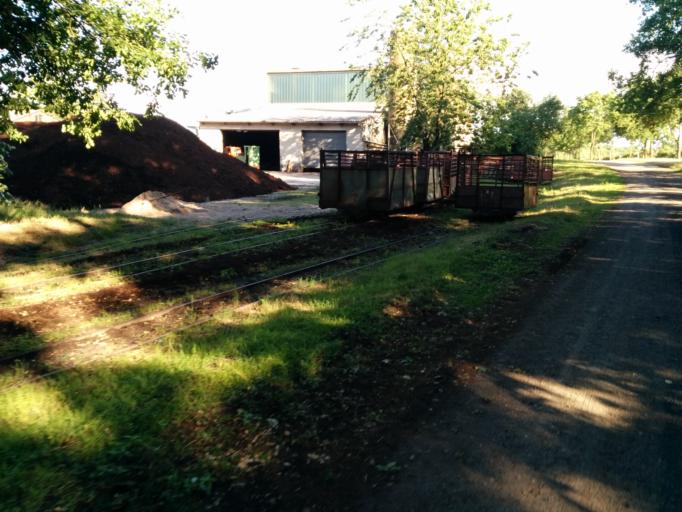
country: DE
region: Lower Saxony
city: Lohne
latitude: 52.6299
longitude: 8.2610
